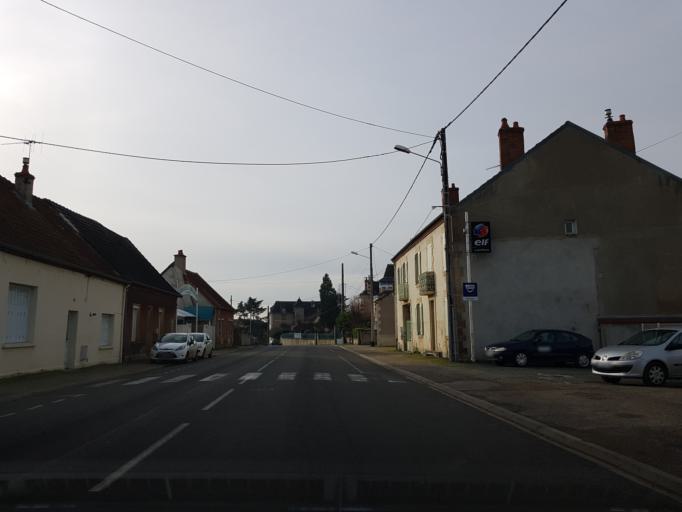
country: FR
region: Auvergne
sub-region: Departement de l'Allier
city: Yzeure
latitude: 46.5722
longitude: 3.3521
